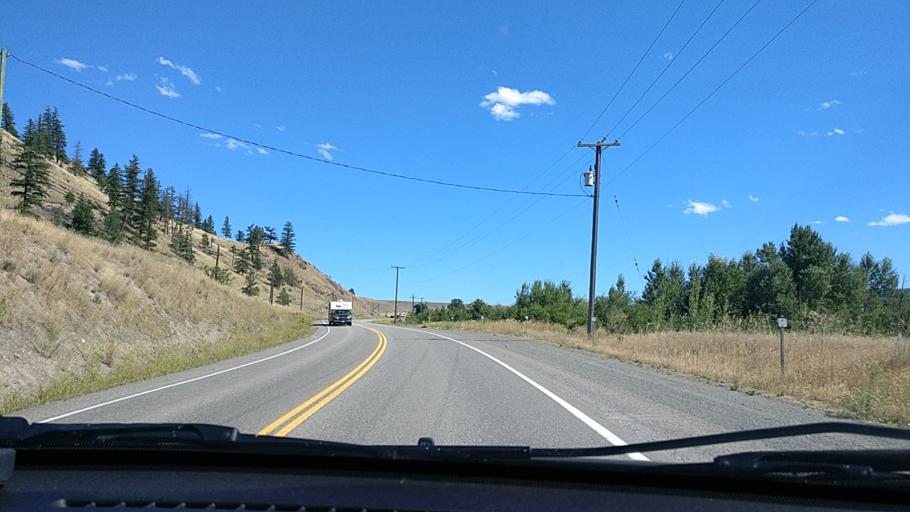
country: CA
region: British Columbia
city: Kamloops
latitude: 50.6658
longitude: -120.5606
